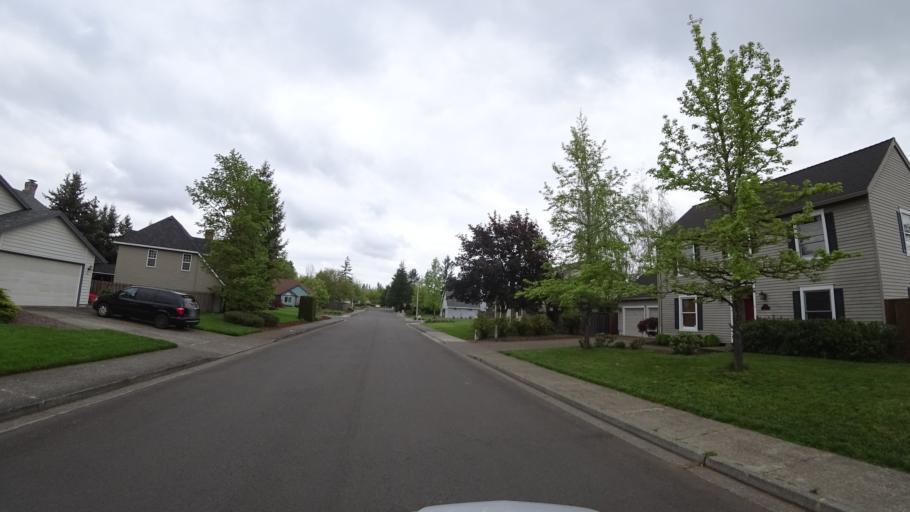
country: US
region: Oregon
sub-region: Washington County
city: Hillsboro
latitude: 45.5375
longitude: -122.9824
